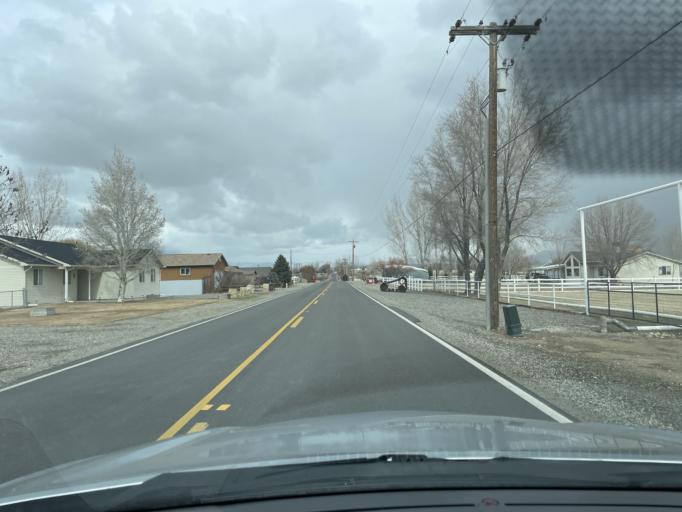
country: US
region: Colorado
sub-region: Mesa County
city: Loma
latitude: 39.1977
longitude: -108.8083
